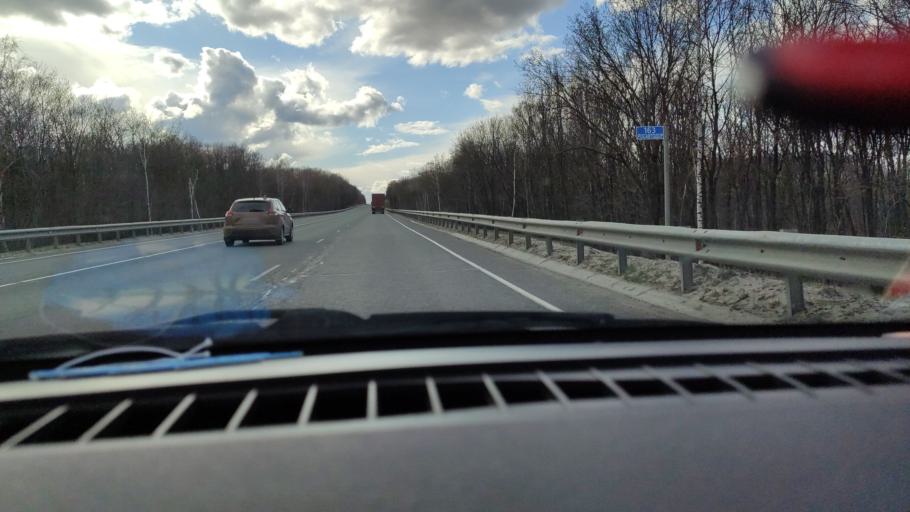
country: RU
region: Saratov
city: Vol'sk
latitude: 52.1069
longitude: 47.4139
